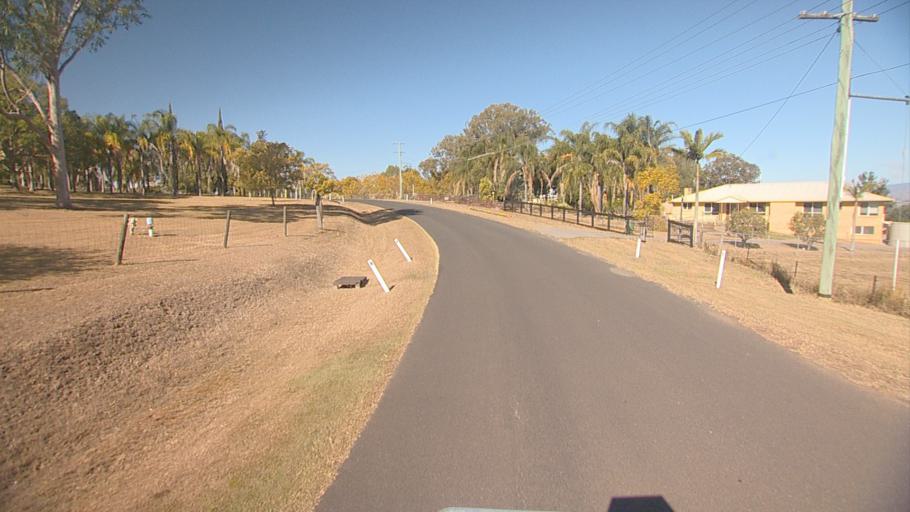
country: AU
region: Queensland
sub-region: Logan
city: Cedar Vale
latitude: -27.8917
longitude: 152.9773
